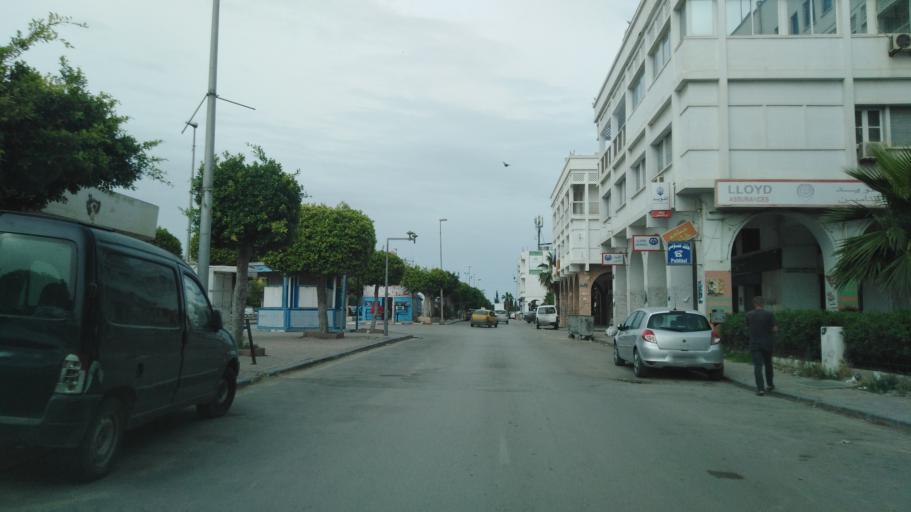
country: TN
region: Safaqis
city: Sfax
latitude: 34.7344
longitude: 10.7628
